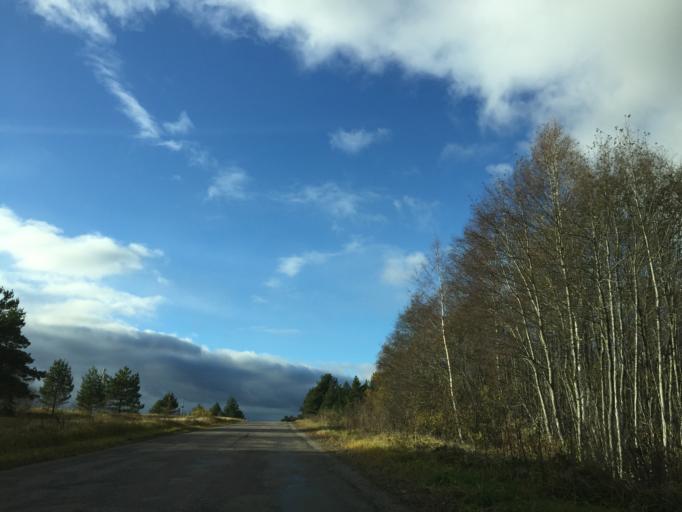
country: LV
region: Kandava
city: Kandava
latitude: 56.9685
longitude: 22.9531
